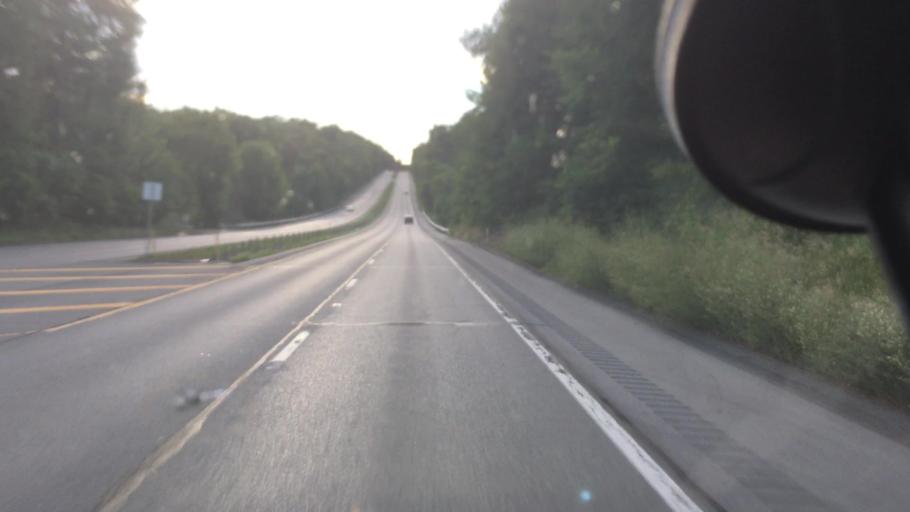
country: US
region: Pennsylvania
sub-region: Beaver County
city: Big Beaver
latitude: 40.7934
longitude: -80.4166
